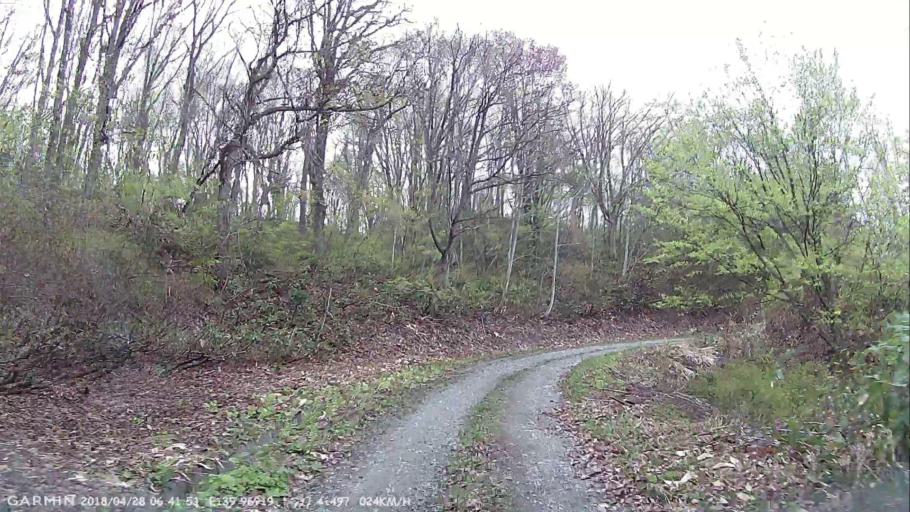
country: JP
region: Fukushima
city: Inawashiro
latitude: 37.4149
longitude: 139.9692
